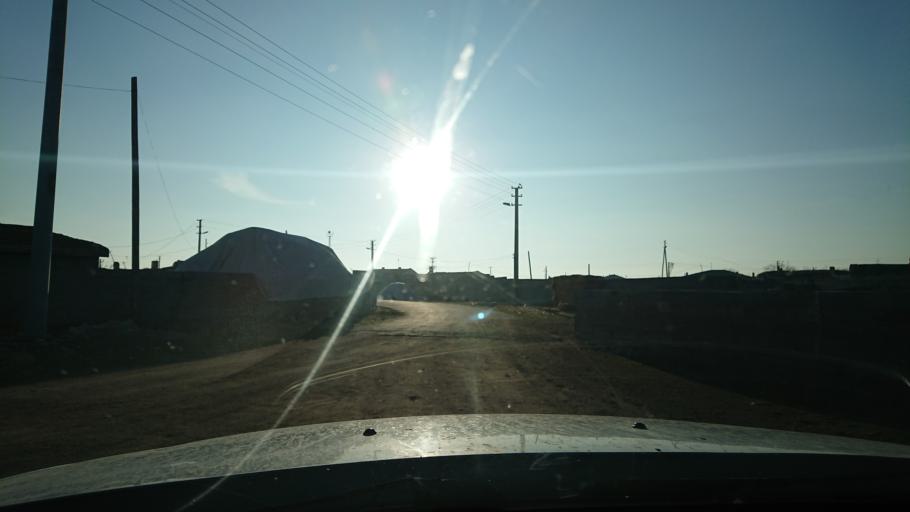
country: TR
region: Aksaray
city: Sultanhani
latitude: 38.2936
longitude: 33.5199
